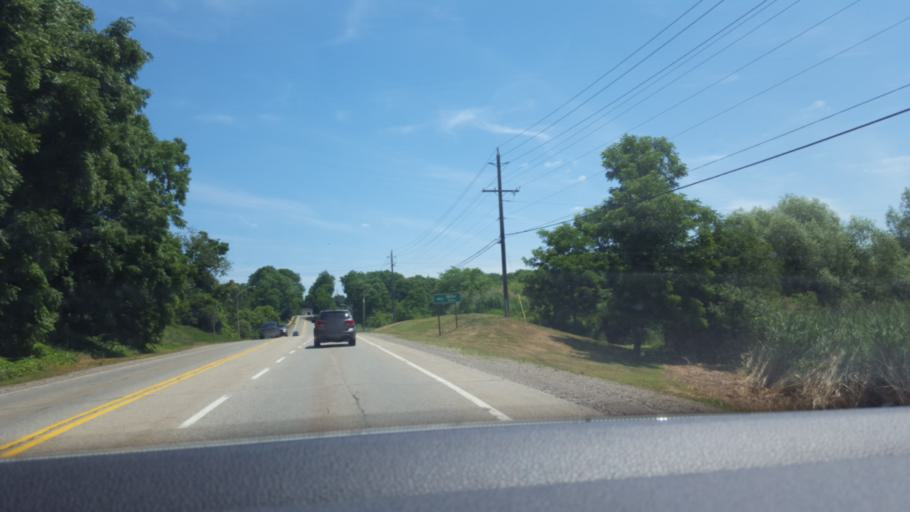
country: CA
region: Ontario
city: Ancaster
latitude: 43.2026
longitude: -79.9770
